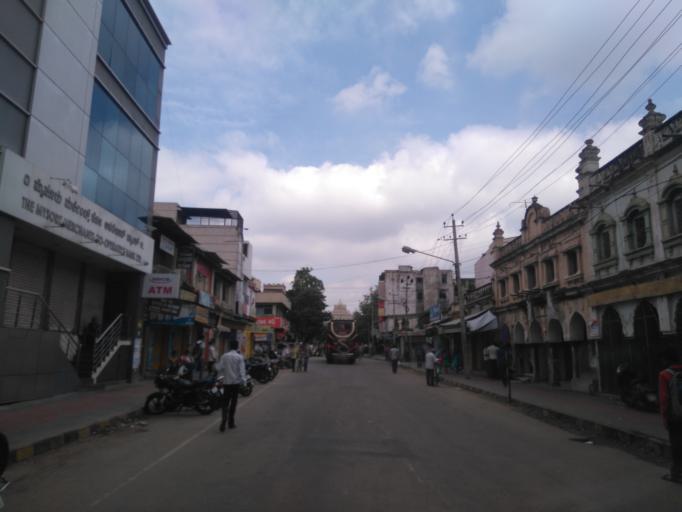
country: IN
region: Karnataka
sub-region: Mysore
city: Mysore
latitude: 12.3065
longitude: 76.6521
